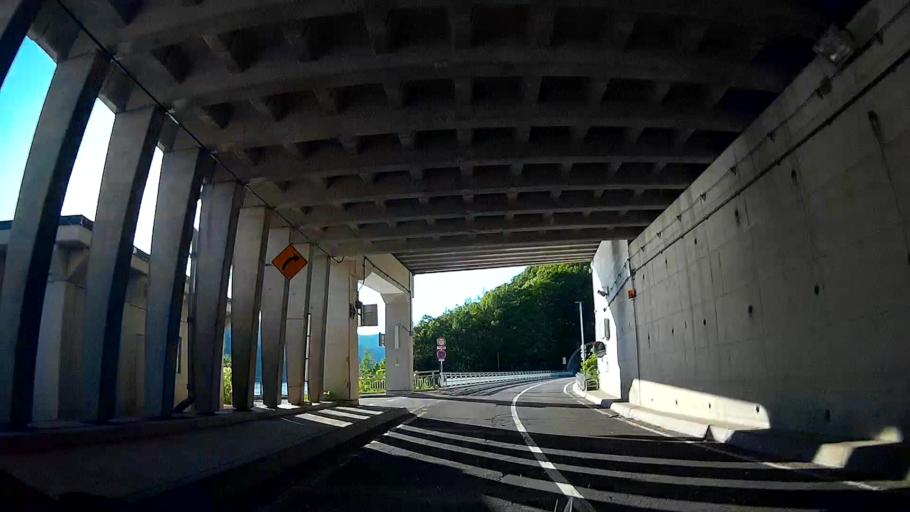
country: JP
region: Hokkaido
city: Sapporo
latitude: 42.9916
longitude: 141.1605
